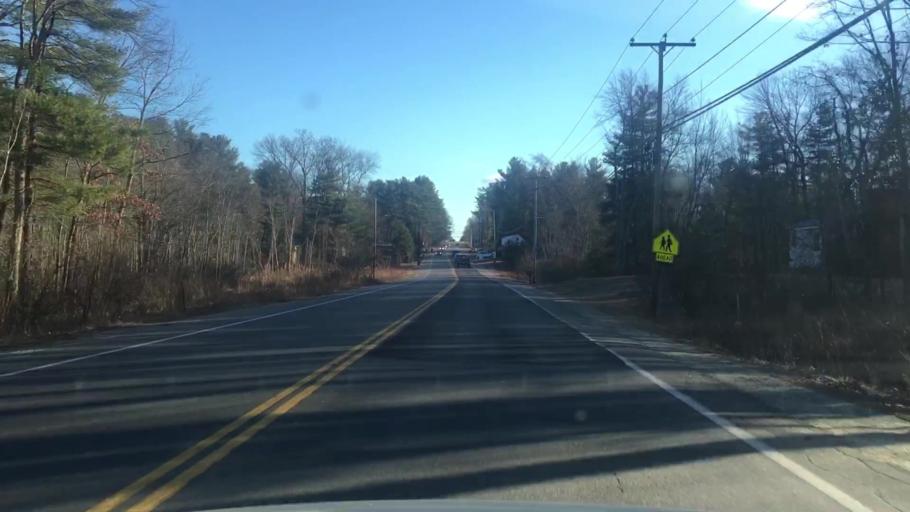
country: US
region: New Hampshire
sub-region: Rockingham County
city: Londonderry
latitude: 42.8777
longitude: -71.3807
